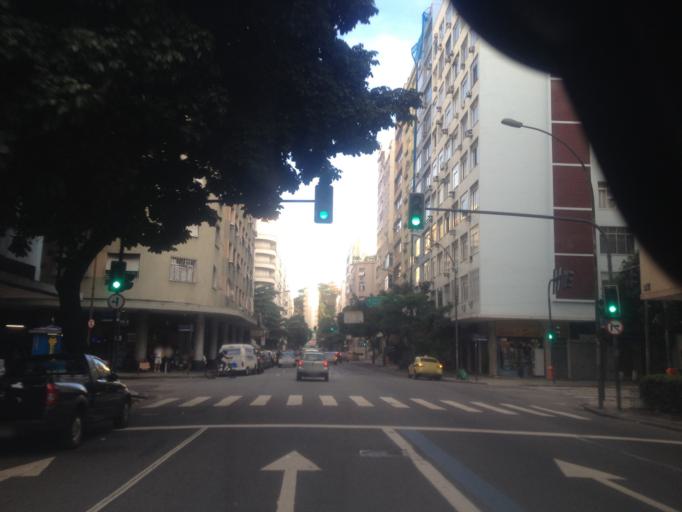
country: BR
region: Rio de Janeiro
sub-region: Rio De Janeiro
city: Rio de Janeiro
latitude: -22.9839
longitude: -43.1917
